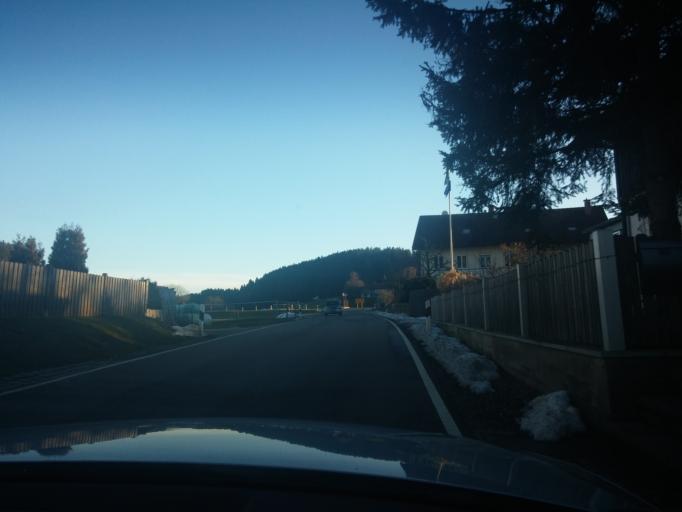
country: DE
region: Bavaria
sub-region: Swabia
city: Altusried
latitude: 47.8100
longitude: 10.1804
